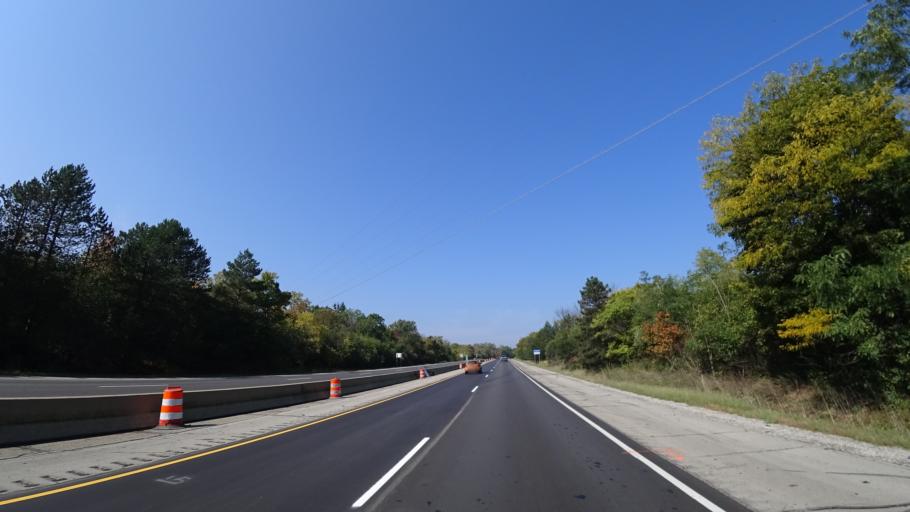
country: US
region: Michigan
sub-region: Washtenaw County
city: Ann Arbor
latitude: 42.2565
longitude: -83.7779
